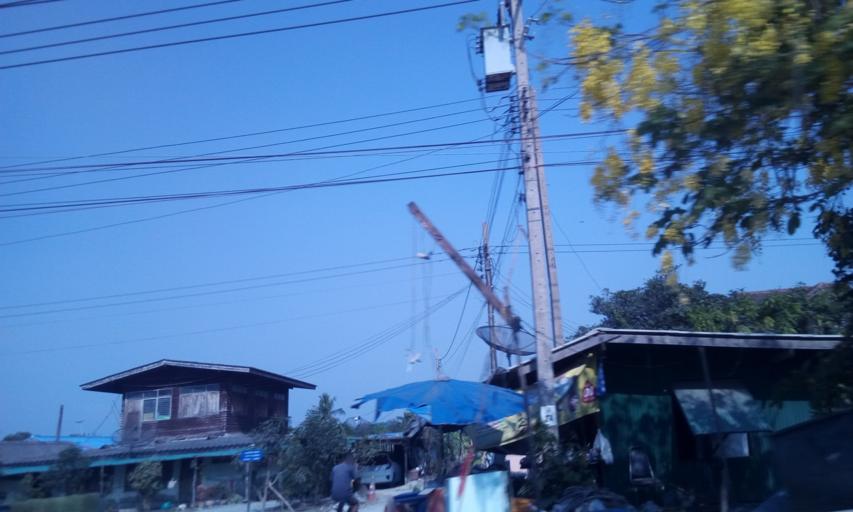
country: TH
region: Nonthaburi
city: Sai Noi
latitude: 14.0321
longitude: 100.3123
